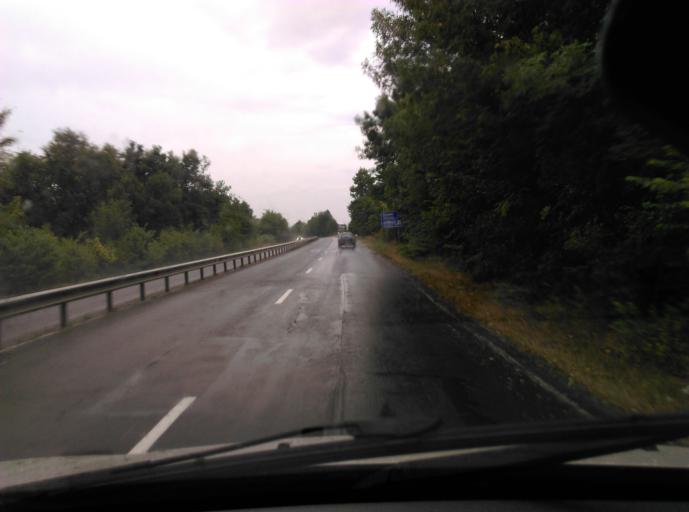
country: BG
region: Burgas
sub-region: Obshtina Burgas
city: Burgas
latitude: 42.4366
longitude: 27.4844
